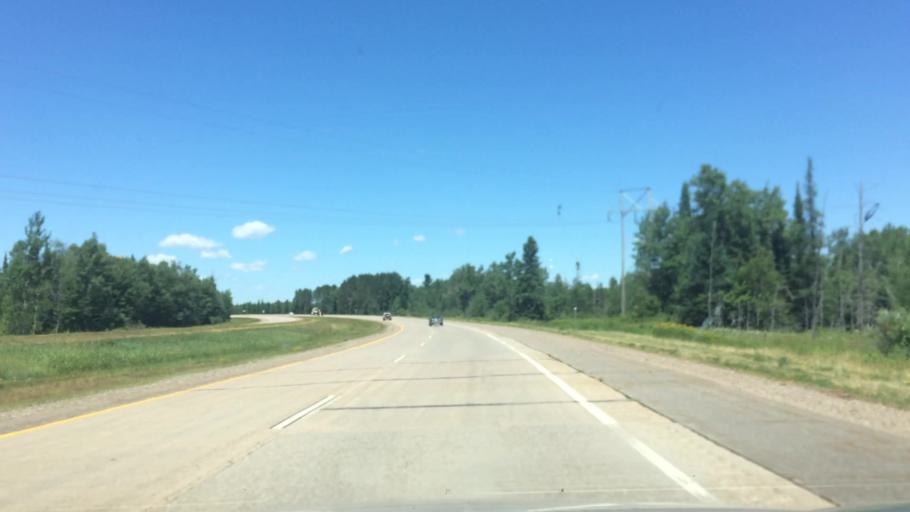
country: US
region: Wisconsin
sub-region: Lincoln County
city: Tomahawk
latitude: 45.3726
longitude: -89.6668
